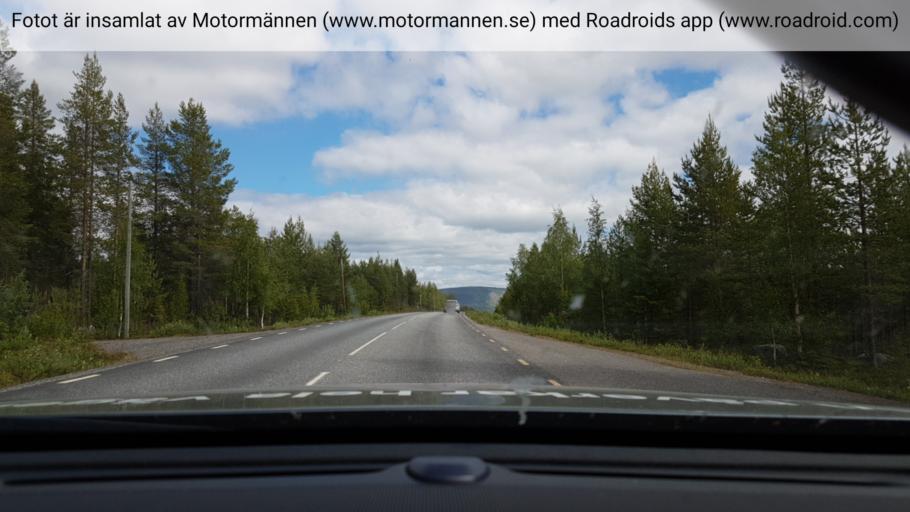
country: SE
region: Vaesterbotten
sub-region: Sorsele Kommun
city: Sorsele
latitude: 65.6846
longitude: 17.2659
